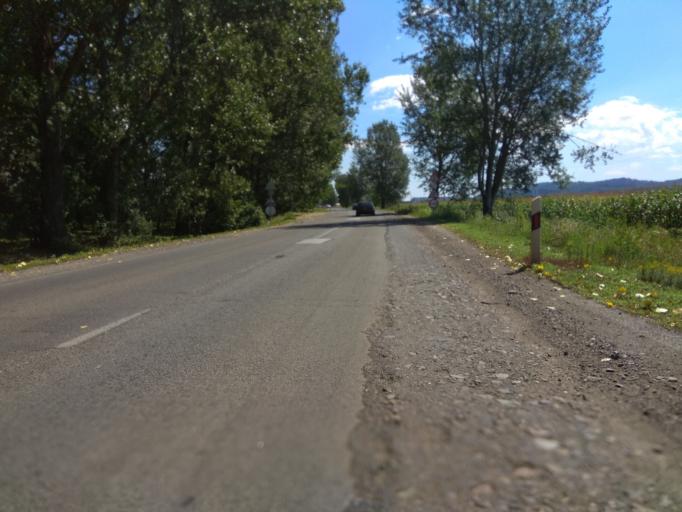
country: HU
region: Borsod-Abauj-Zemplen
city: Sajokaza
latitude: 48.2669
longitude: 20.5980
